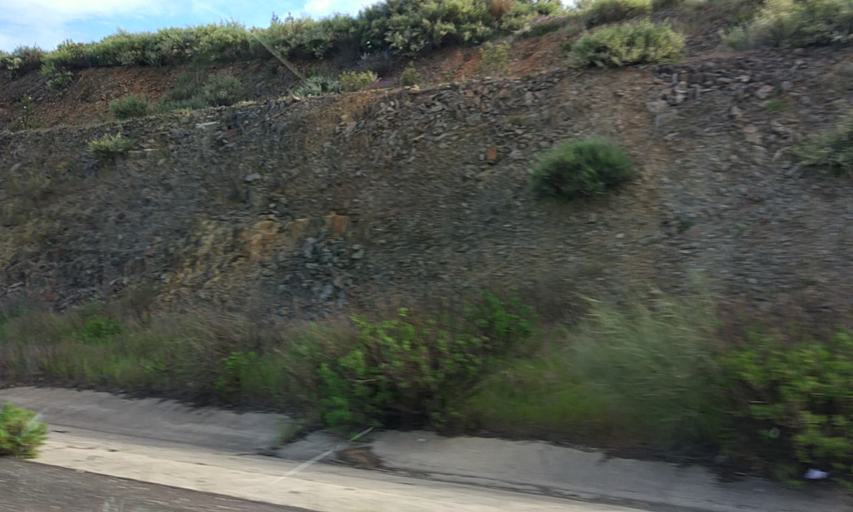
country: ES
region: Extremadura
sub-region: Provincia de Caceres
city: Casas de Don Gomez
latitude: 40.0238
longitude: -6.6010
